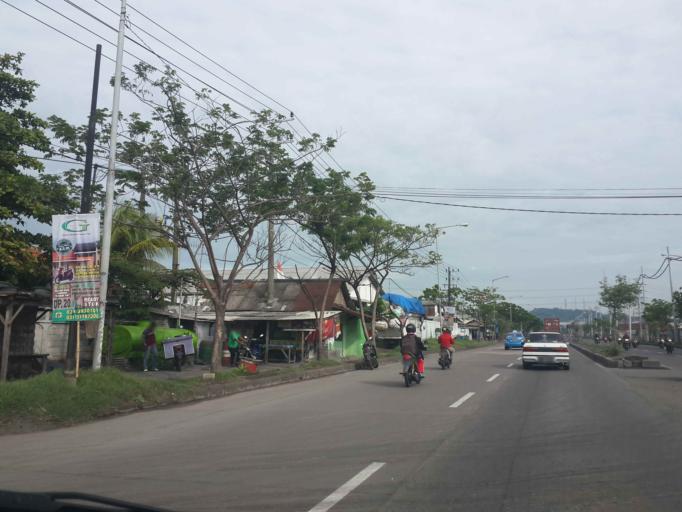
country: ID
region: East Java
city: Kebomas
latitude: -7.2038
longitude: 112.6499
